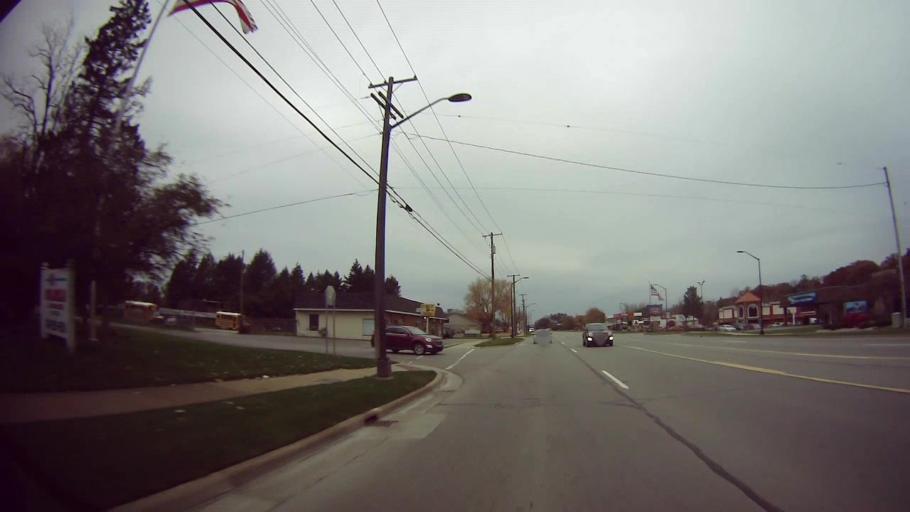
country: US
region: Michigan
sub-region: Oakland County
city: Waterford
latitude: 42.7140
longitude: -83.4112
